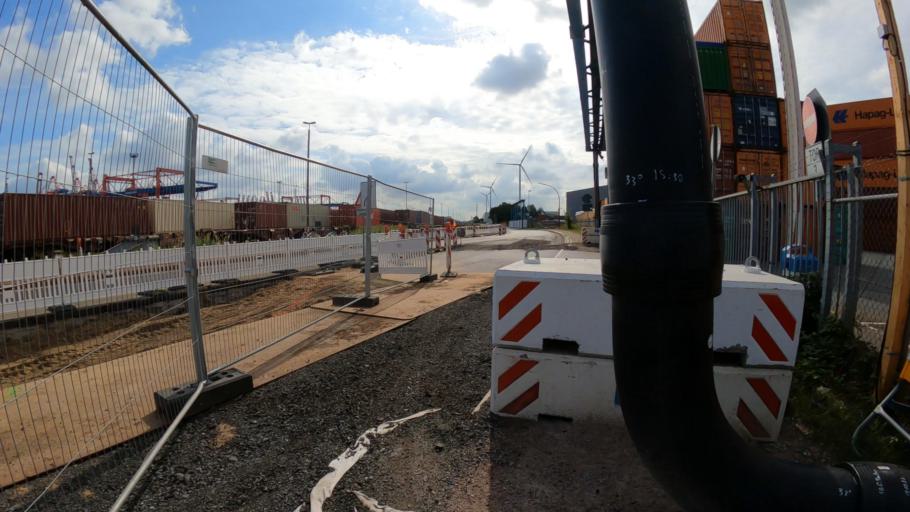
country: DE
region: Hamburg
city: Altona
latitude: 53.5305
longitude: 9.8956
